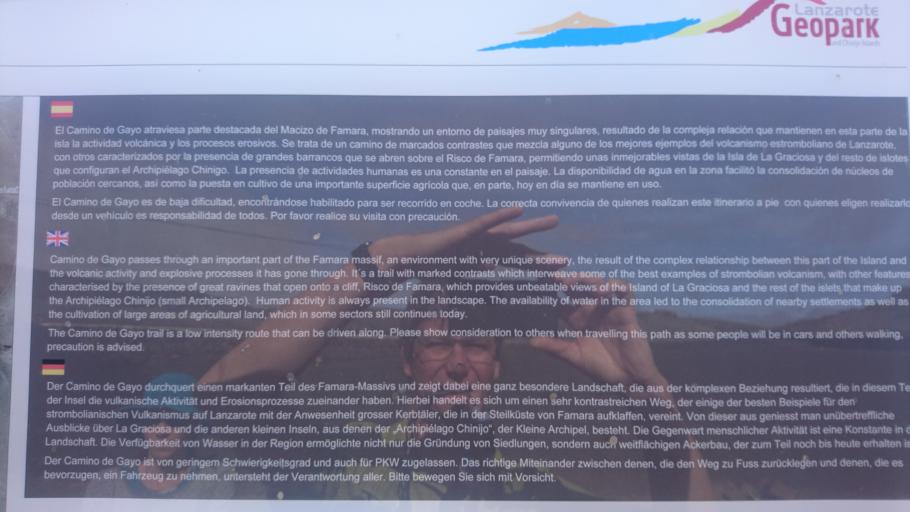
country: ES
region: Canary Islands
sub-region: Provincia de Las Palmas
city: Haria
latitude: 29.1783
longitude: -13.4917
